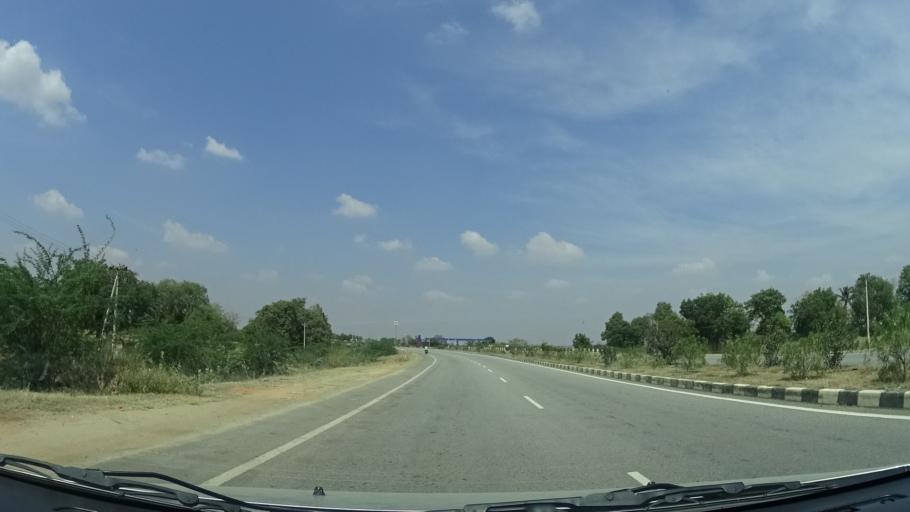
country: IN
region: Andhra Pradesh
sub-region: Anantapur
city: Dharmavaram
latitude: 14.2880
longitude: 77.6278
